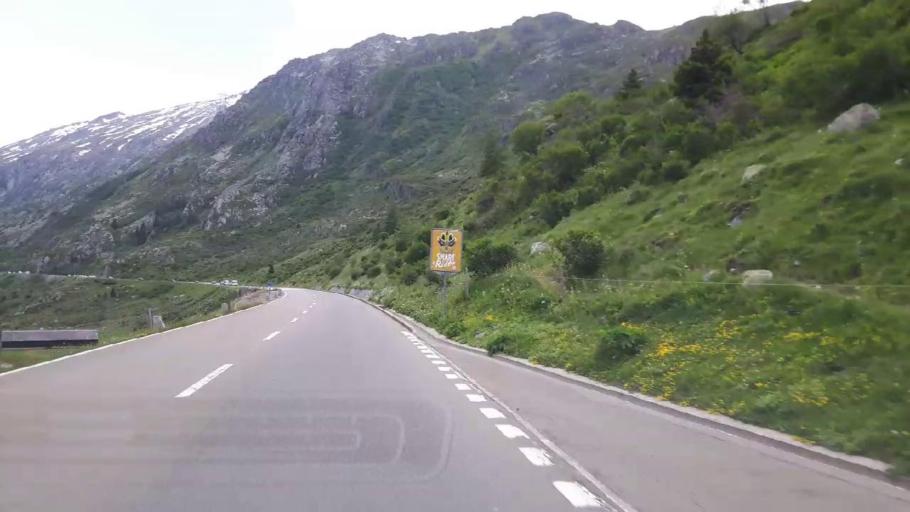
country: CH
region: Uri
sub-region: Uri
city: Andermatt
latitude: 46.6091
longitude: 8.5700
